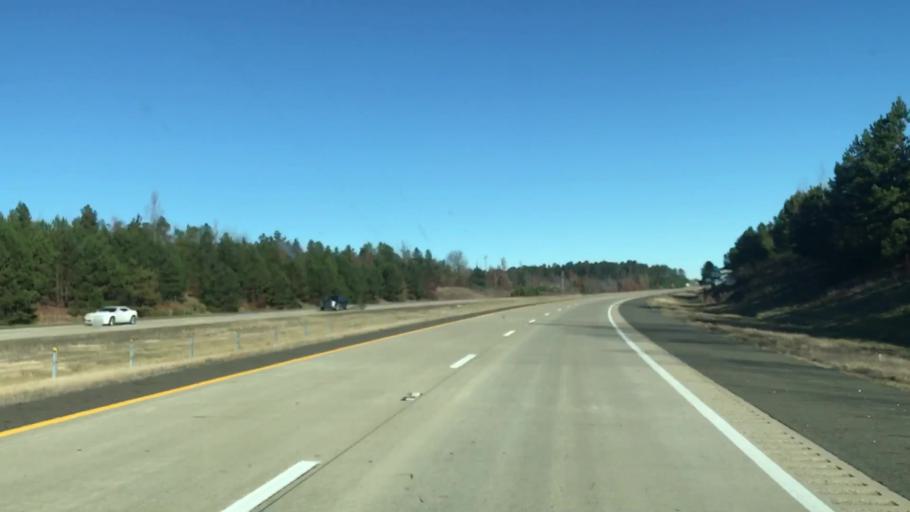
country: US
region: Louisiana
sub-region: Caddo Parish
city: Vivian
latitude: 33.1051
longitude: -93.8957
